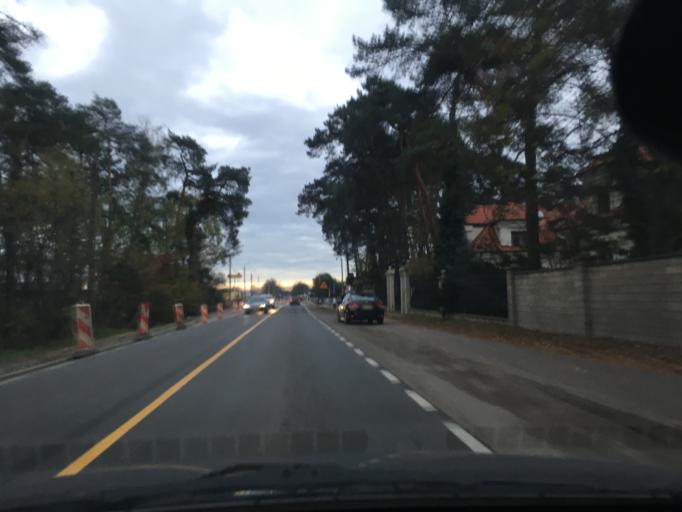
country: PL
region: Masovian Voivodeship
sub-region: Powiat piaseczynski
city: Lesznowola
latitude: 52.0972
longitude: 20.9165
